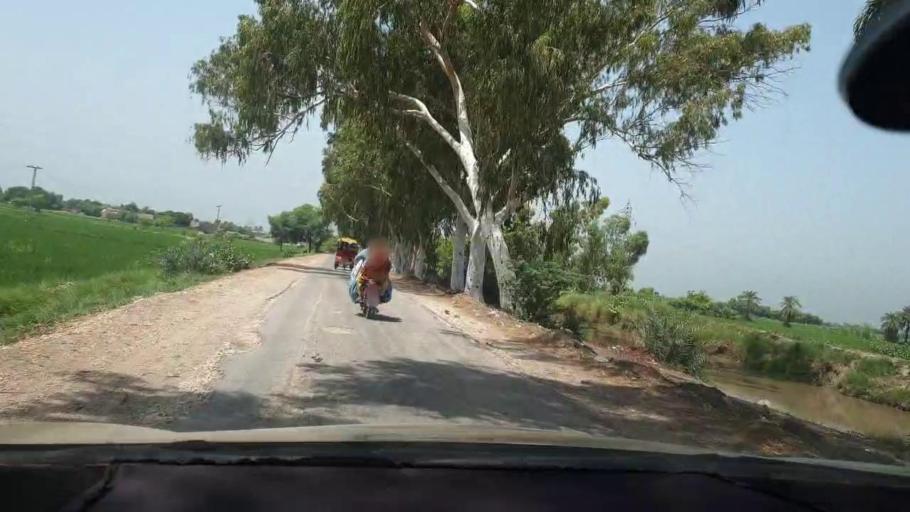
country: PK
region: Sindh
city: Kambar
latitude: 27.6340
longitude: 67.9864
